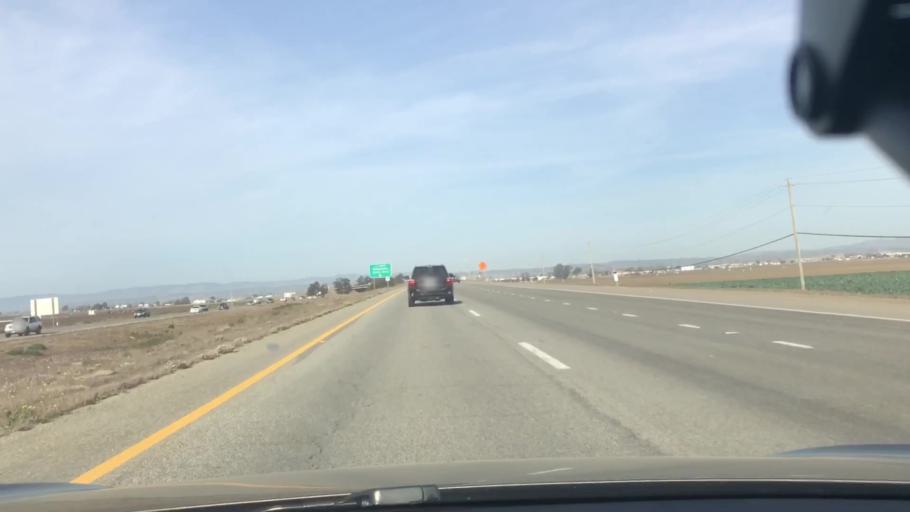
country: US
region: California
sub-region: Monterey County
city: Castroville
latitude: 36.7470
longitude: -121.7702
